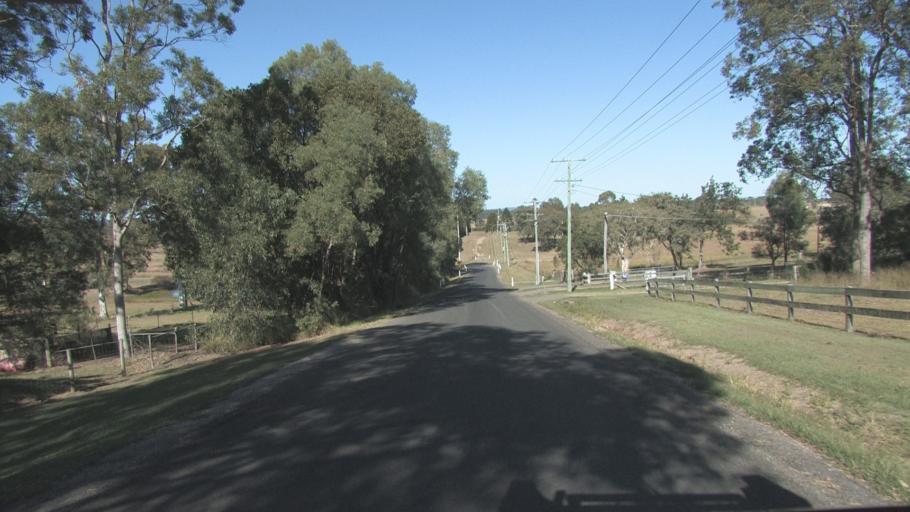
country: AU
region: Queensland
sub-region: Logan
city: Chambers Flat
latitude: -27.7578
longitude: 153.0692
